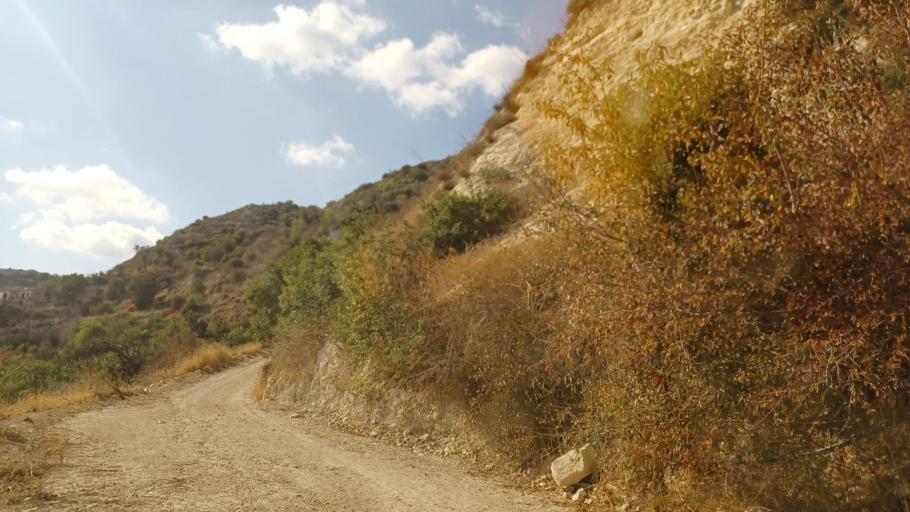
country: CY
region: Pafos
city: Pegeia
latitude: 34.9158
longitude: 32.4553
